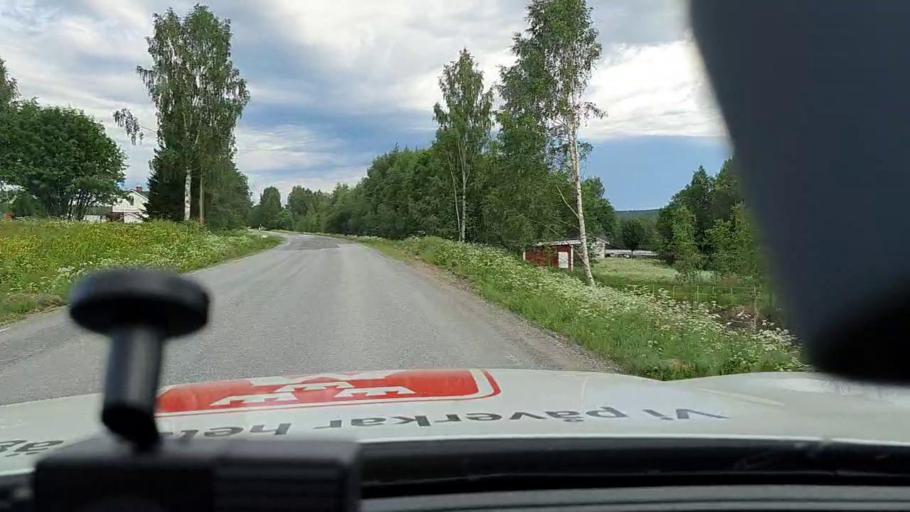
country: SE
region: Norrbotten
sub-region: Bodens Kommun
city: Saevast
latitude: 65.7683
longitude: 21.6899
